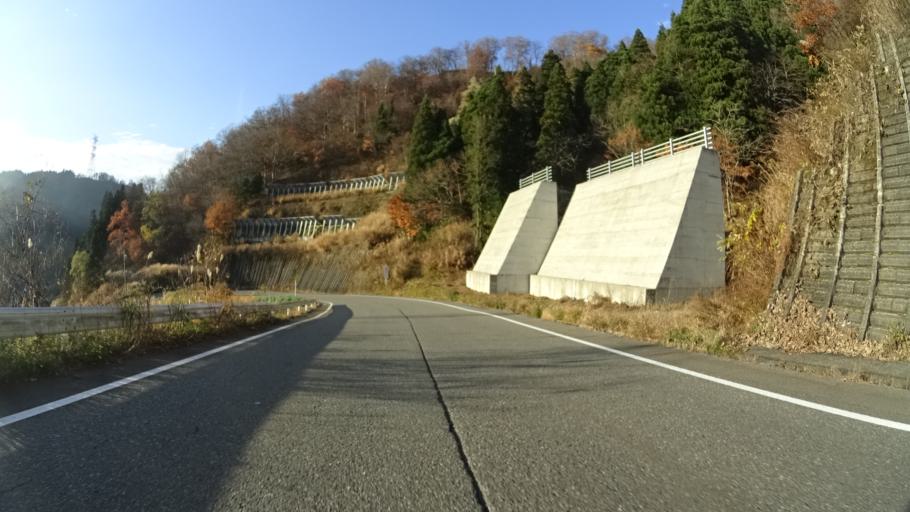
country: JP
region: Niigata
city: Shiozawa
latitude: 36.9861
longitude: 138.7472
